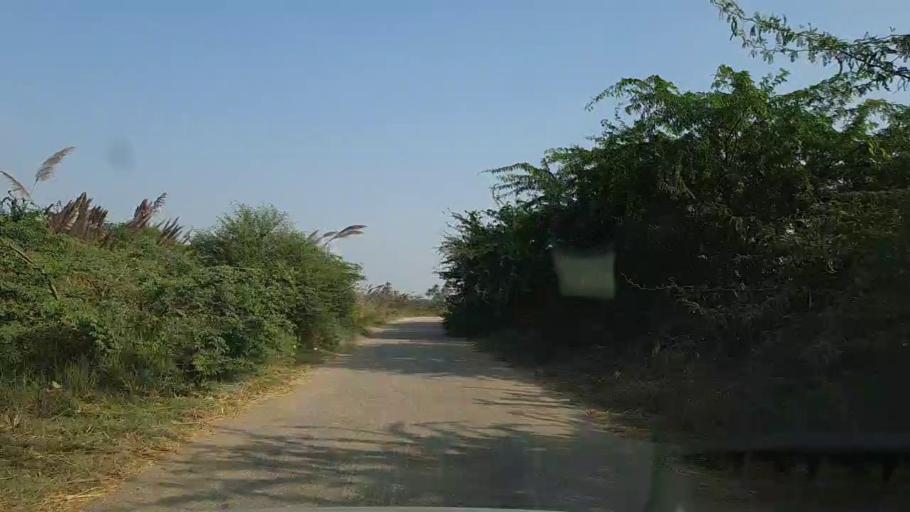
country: PK
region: Sindh
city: Mirpur Sakro
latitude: 24.5944
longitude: 67.6047
